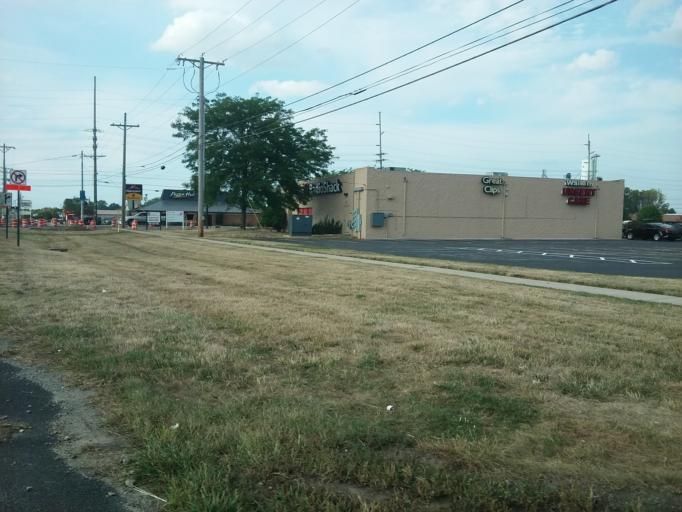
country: US
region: Ohio
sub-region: Wood County
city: Bowling Green
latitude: 41.3559
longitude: -83.6501
